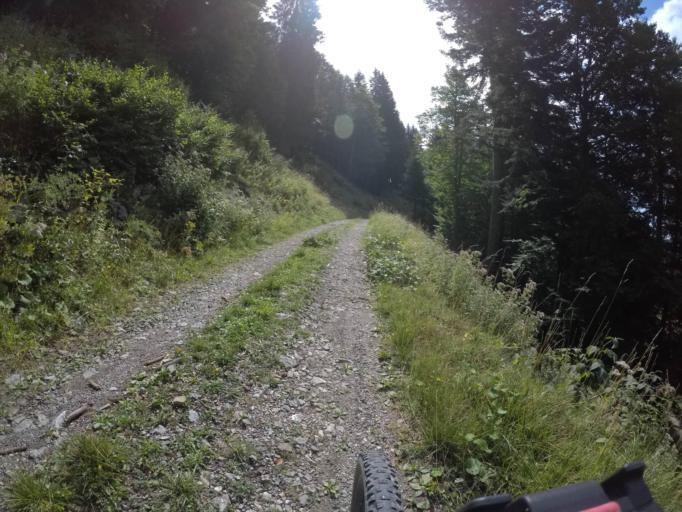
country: IT
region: Friuli Venezia Giulia
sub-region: Provincia di Udine
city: Paularo
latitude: 46.5124
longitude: 13.1962
